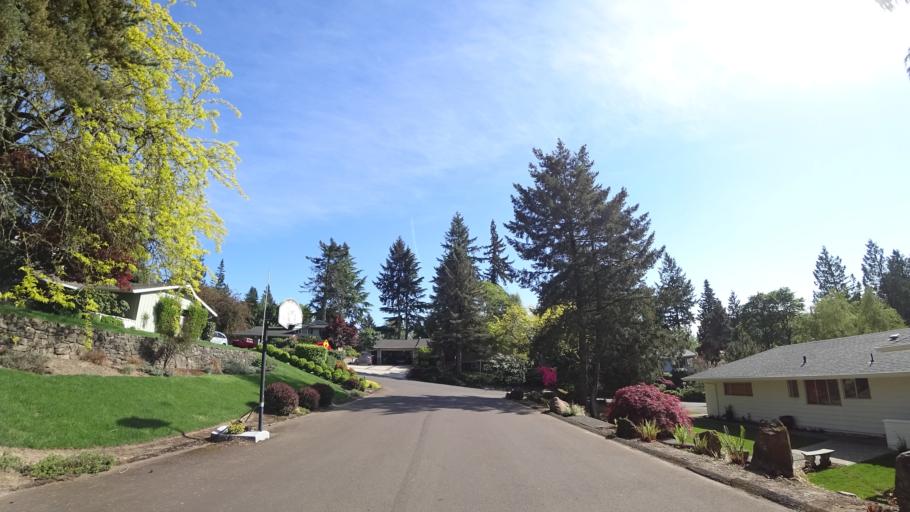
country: US
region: Oregon
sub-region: Washington County
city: West Slope
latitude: 45.4951
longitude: -122.7444
